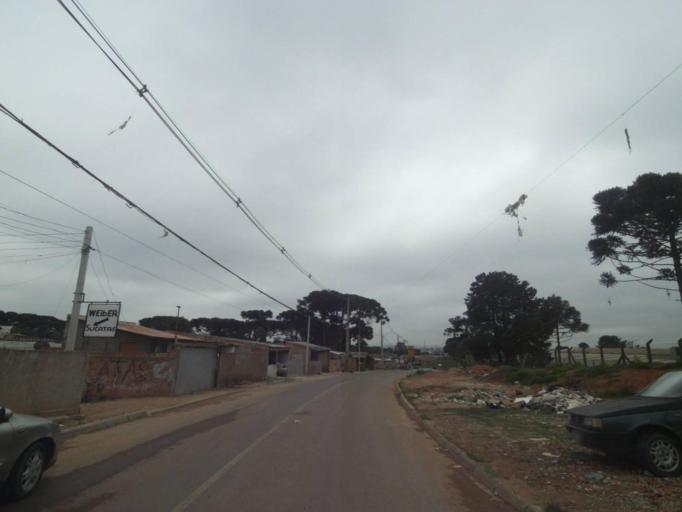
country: BR
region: Parana
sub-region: Araucaria
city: Araucaria
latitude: -25.5068
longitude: -49.3511
